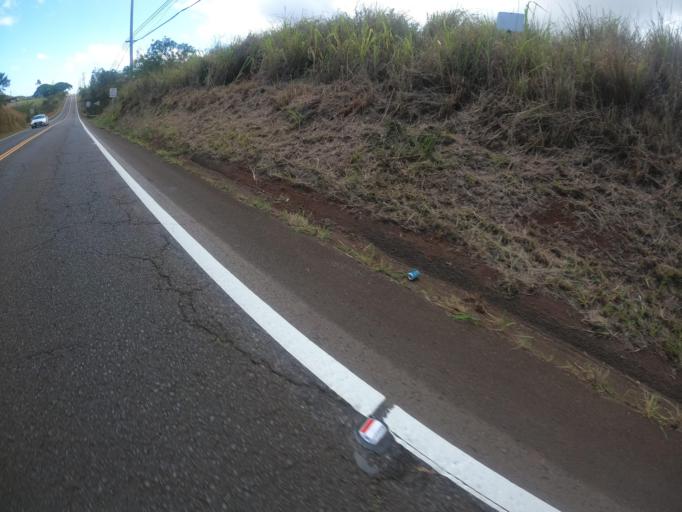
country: US
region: Hawaii
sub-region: Honolulu County
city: Village Park
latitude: 21.4365
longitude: -158.0584
